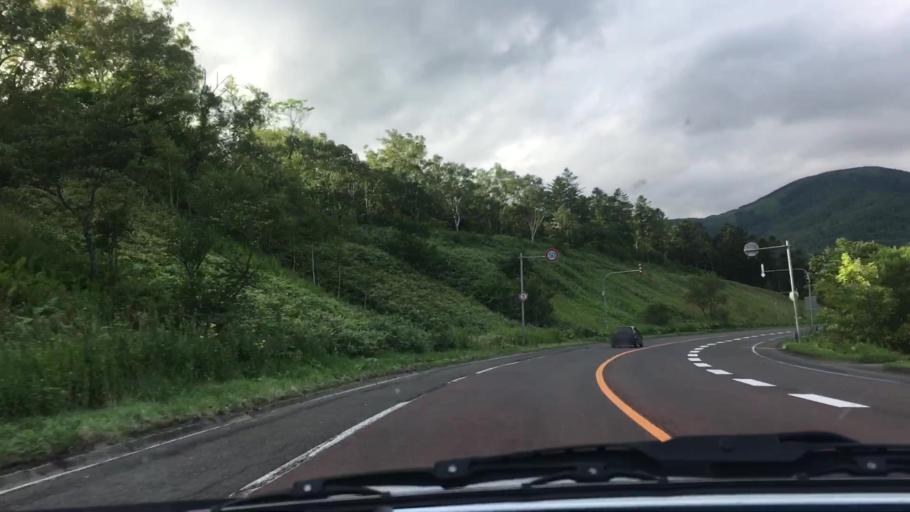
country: JP
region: Hokkaido
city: Shimo-furano
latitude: 43.1291
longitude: 142.7587
